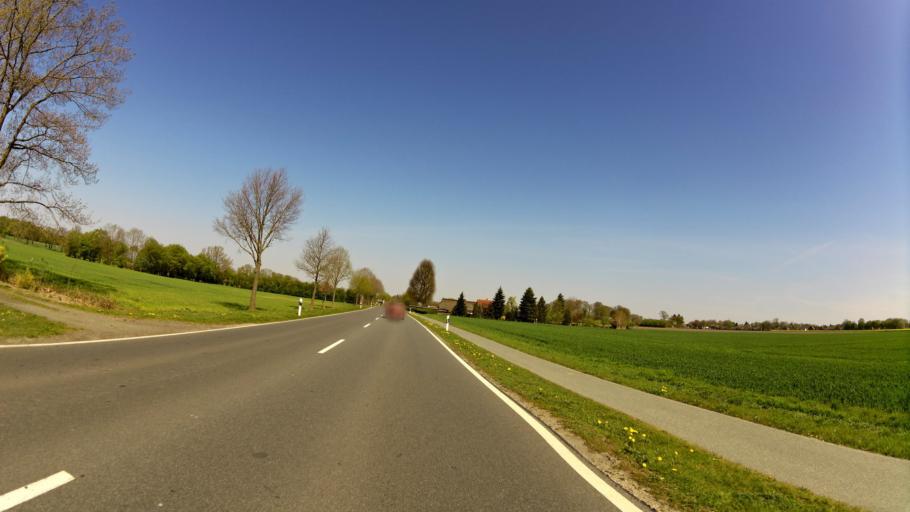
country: DE
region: Lower Saxony
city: Ganderkesee
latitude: 53.0805
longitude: 8.5260
